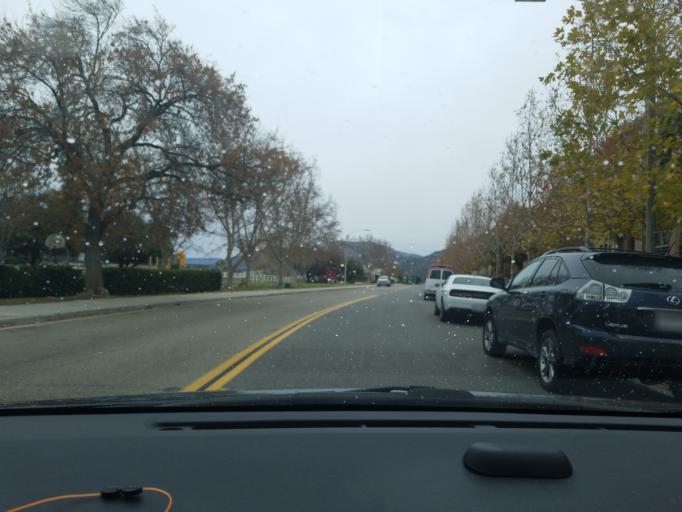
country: US
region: California
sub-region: Riverside County
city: Temecula
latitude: 33.4891
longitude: -117.1479
